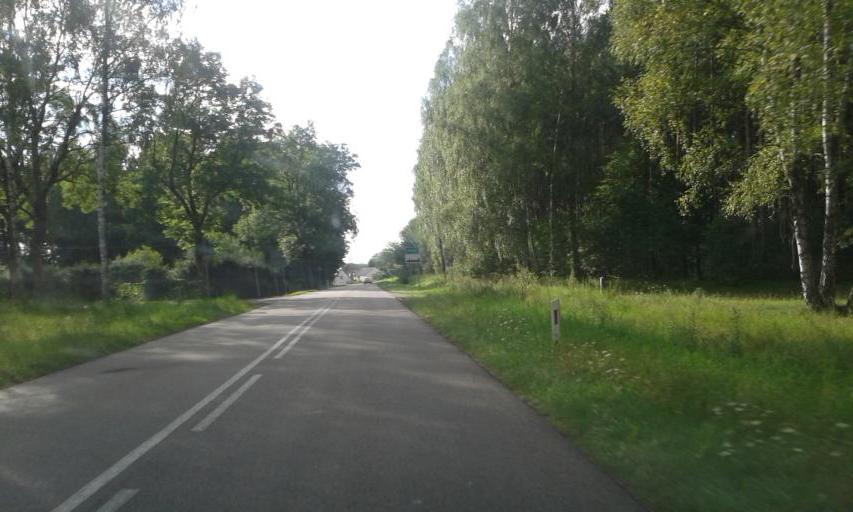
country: PL
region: West Pomeranian Voivodeship
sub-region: Powiat szczecinecki
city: Barwice
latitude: 53.7558
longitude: 16.2606
